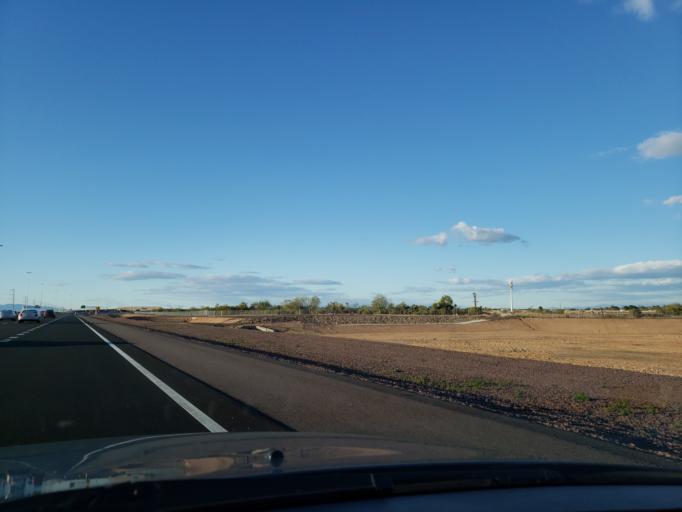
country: US
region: Arizona
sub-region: Maricopa County
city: Laveen
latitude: 33.3396
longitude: -112.1822
